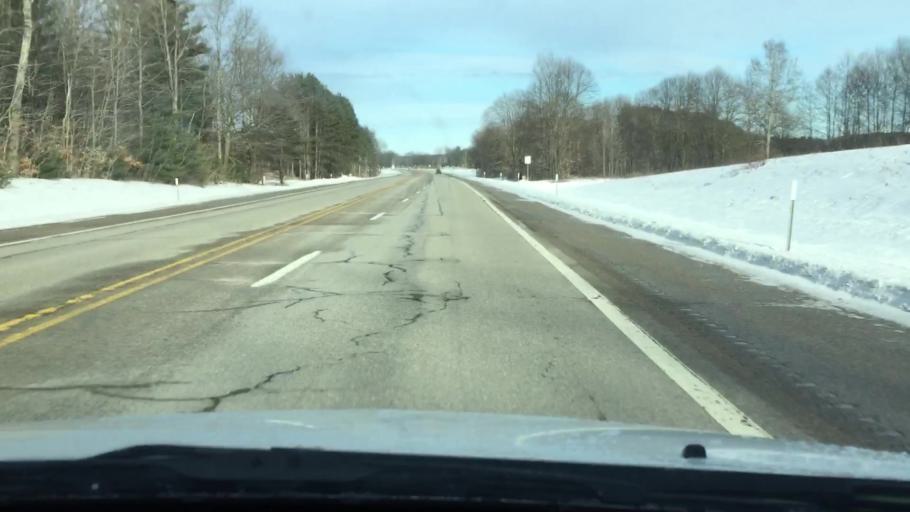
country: US
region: Michigan
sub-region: Kalkaska County
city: Kalkaska
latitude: 44.6083
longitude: -85.3180
